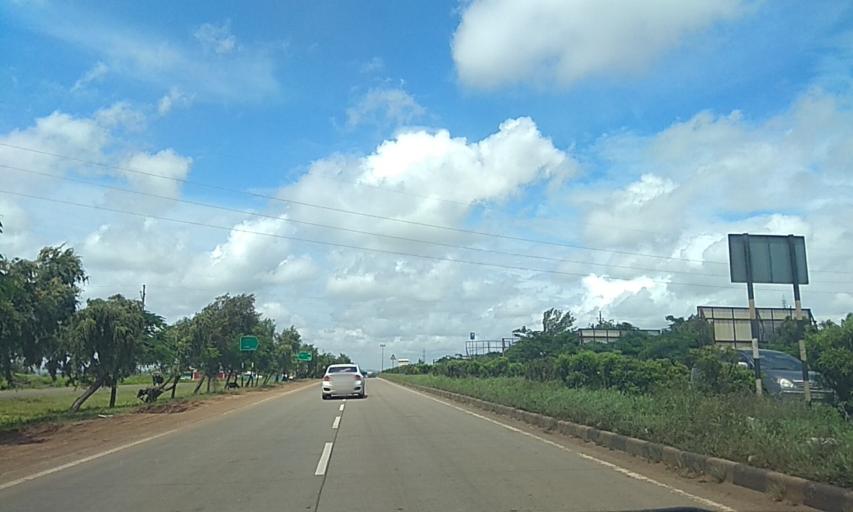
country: IN
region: Karnataka
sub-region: Belgaum
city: Sankeshwar
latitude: 16.1457
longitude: 74.5170
